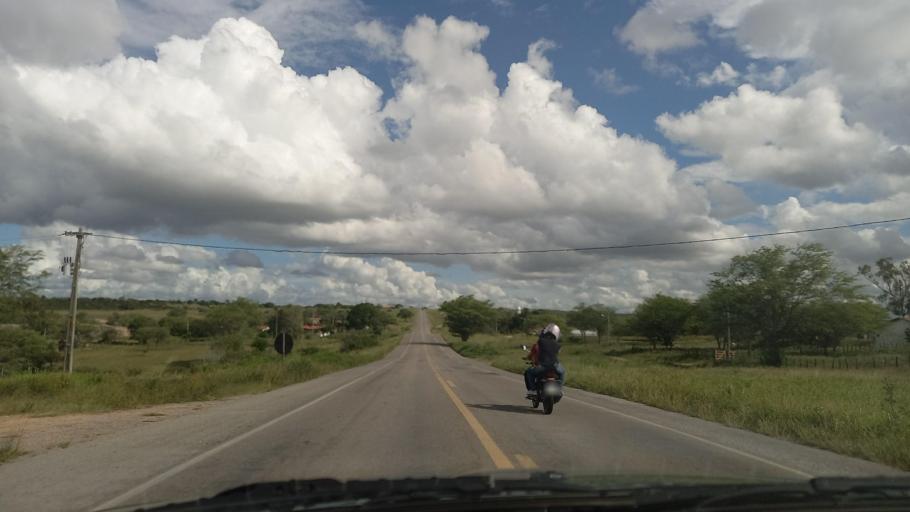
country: BR
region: Pernambuco
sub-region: Lajedo
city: Lajedo
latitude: -8.6206
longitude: -36.3003
